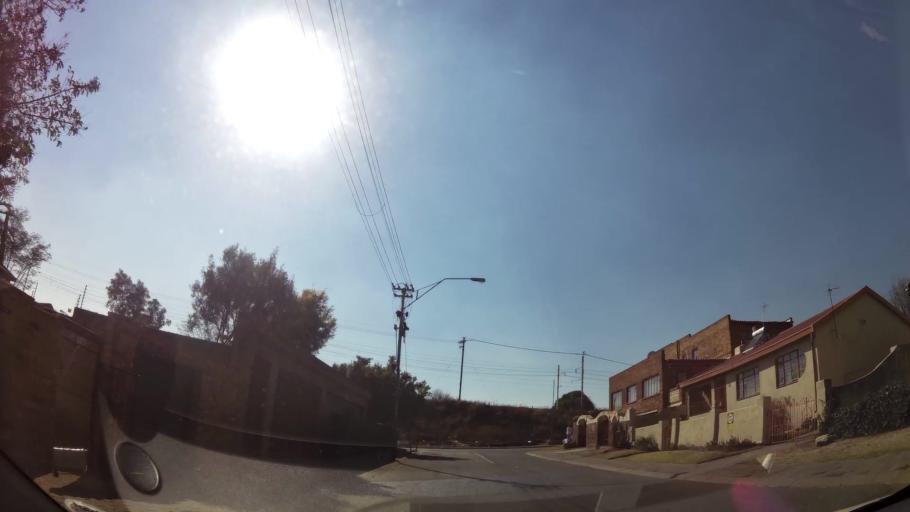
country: ZA
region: Gauteng
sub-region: City of Johannesburg Metropolitan Municipality
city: Johannesburg
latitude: -26.1883
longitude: 27.9664
